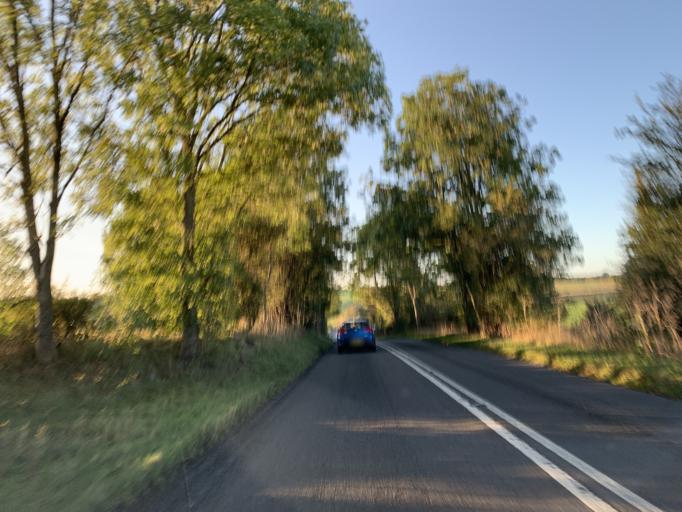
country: GB
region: England
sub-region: Wiltshire
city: Woodford
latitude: 51.1433
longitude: -1.8586
